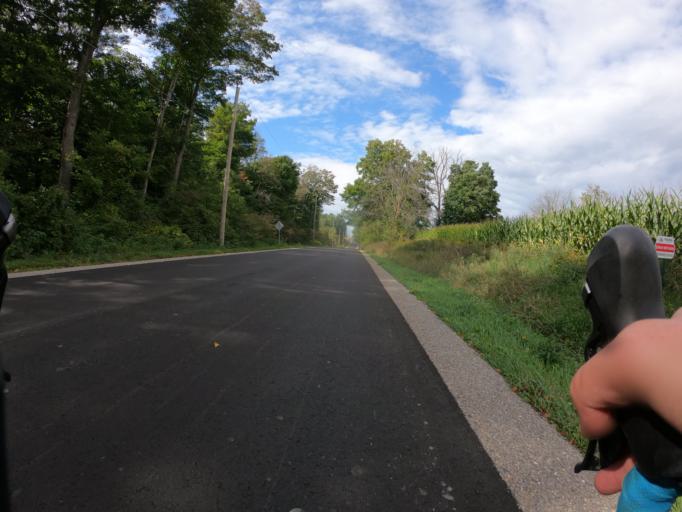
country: CA
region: Ontario
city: Kitchener
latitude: 43.3760
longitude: -80.6170
